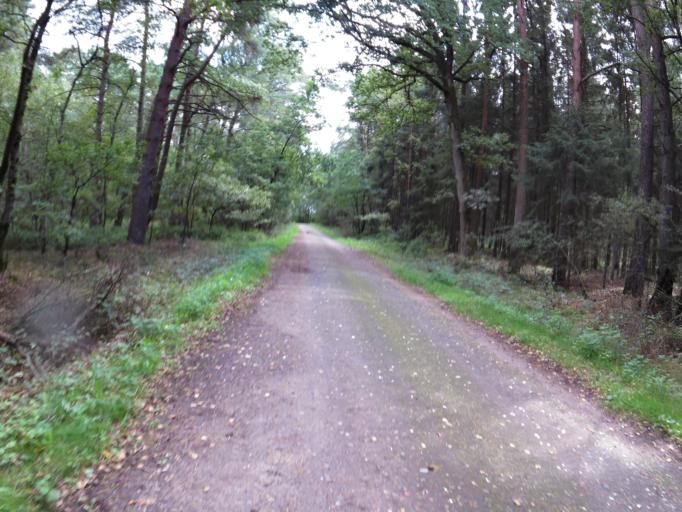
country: DE
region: Lower Saxony
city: Sandbostel
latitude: 53.3678
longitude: 9.1563
